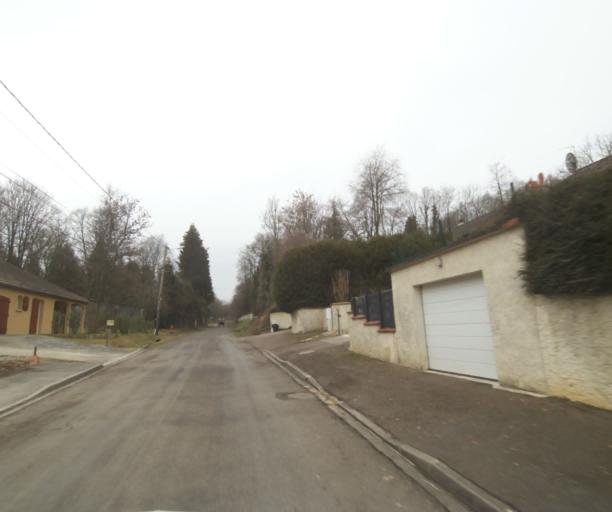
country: FR
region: Champagne-Ardenne
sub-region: Departement de la Haute-Marne
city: Bienville
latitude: 48.5812
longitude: 5.0345
